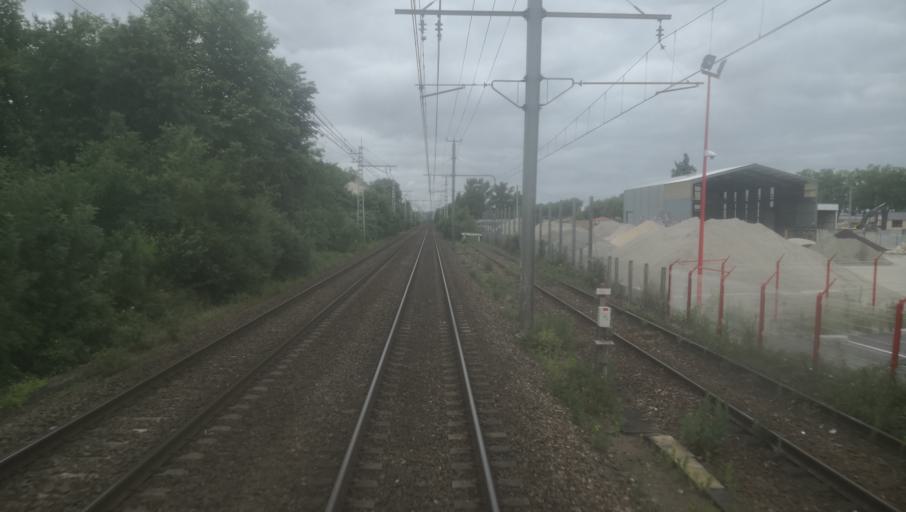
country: FR
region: Midi-Pyrenees
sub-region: Departement de la Haute-Garonne
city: Lespinasse
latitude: 43.7226
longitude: 1.3804
